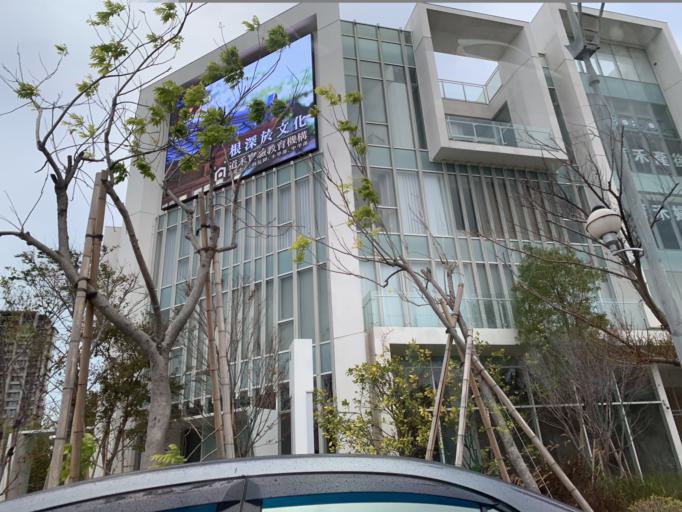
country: TW
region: Taiwan
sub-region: Hsinchu
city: Zhubei
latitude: 24.8154
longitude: 121.0195
